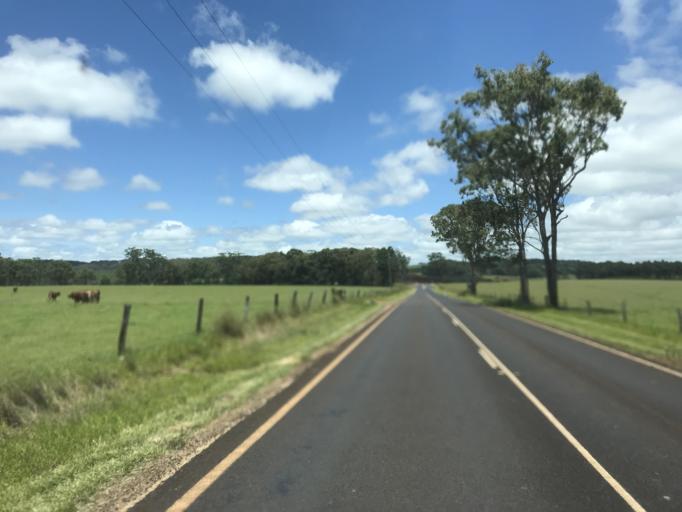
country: AU
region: Queensland
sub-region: Tablelands
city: Ravenshoe
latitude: -17.5115
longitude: 145.4527
